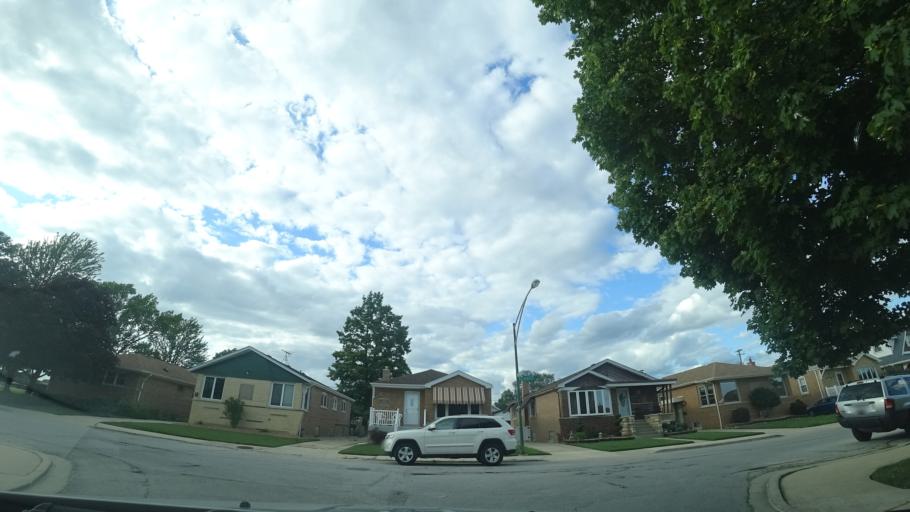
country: US
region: Illinois
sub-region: Cook County
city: Merrionette Park
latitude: 41.6876
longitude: -87.7148
